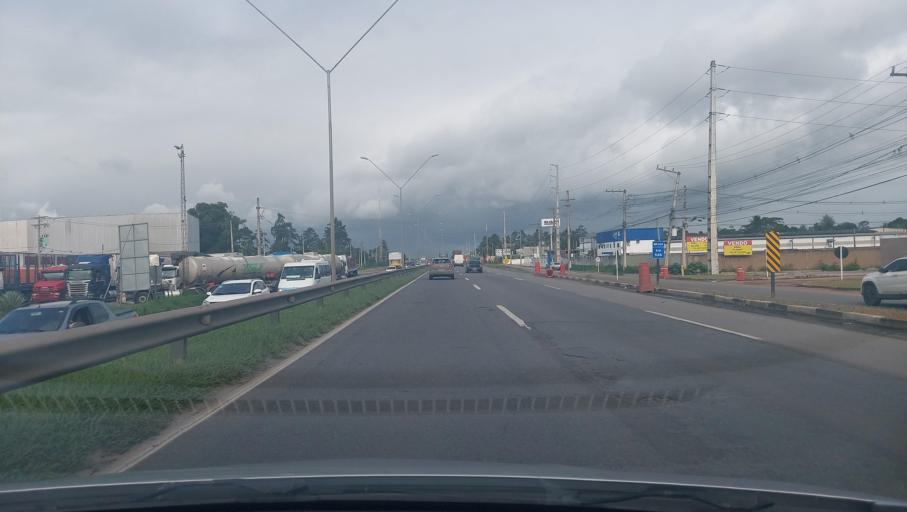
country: BR
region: Bahia
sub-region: Feira De Santana
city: Feira de Santana
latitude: -12.3154
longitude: -38.8785
